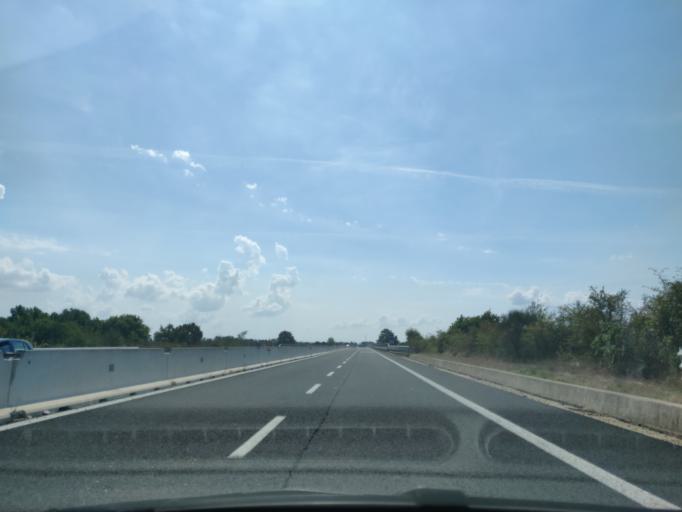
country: IT
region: Latium
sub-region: Provincia di Viterbo
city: Blera
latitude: 42.3365
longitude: 11.9839
